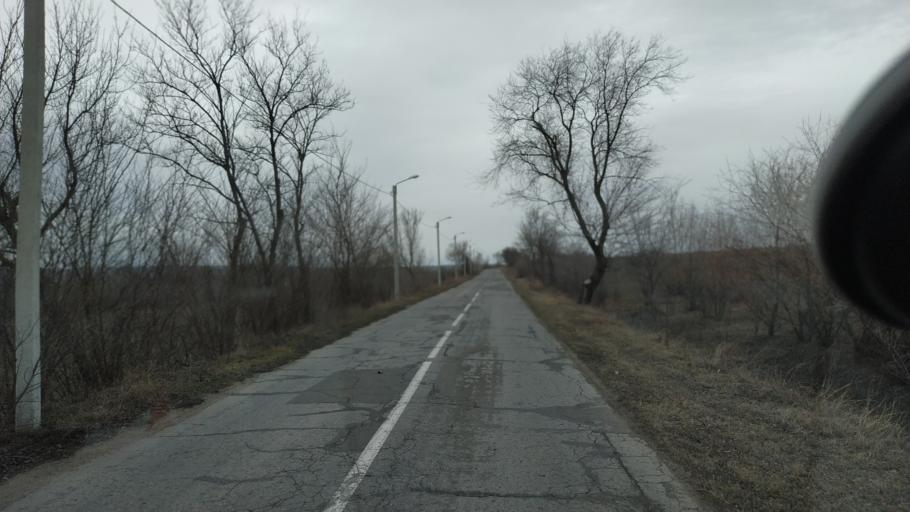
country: MD
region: Telenesti
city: Cocieri
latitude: 47.3253
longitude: 29.0971
